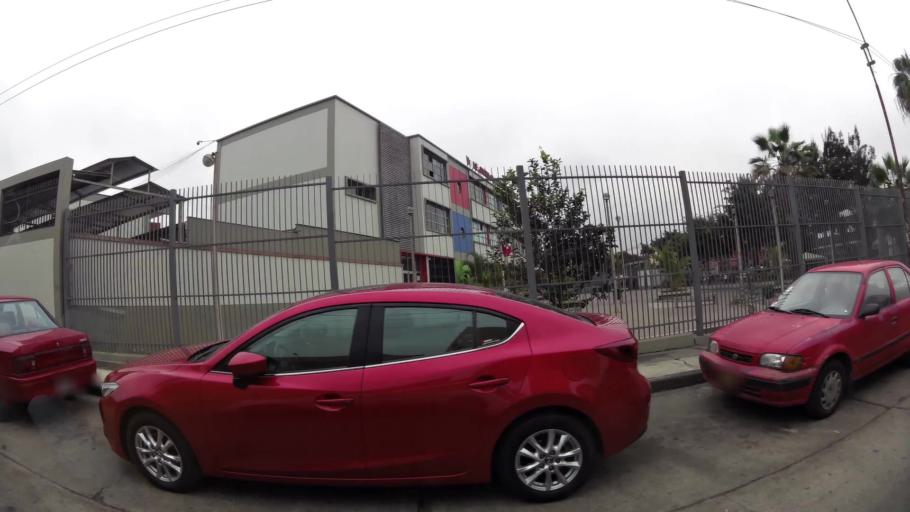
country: PE
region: Lima
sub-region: Lima
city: Surco
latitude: -12.1273
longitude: -77.0094
